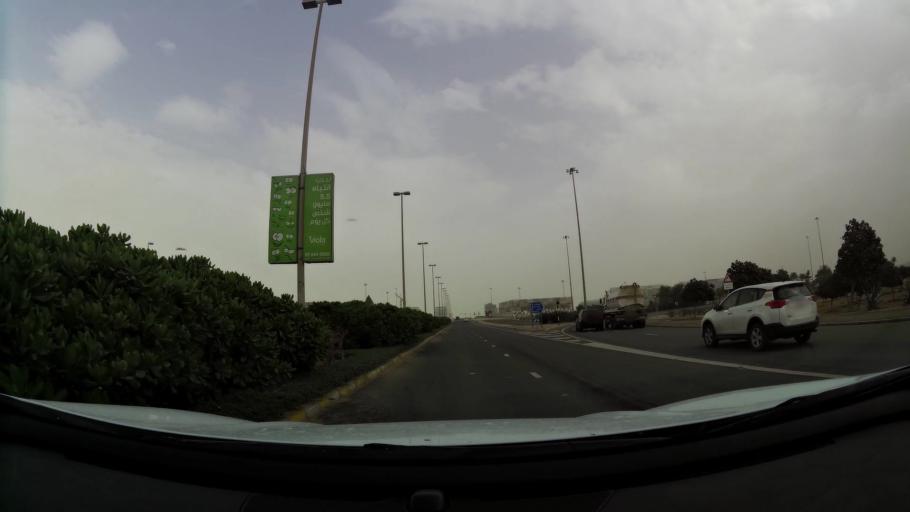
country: AE
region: Abu Dhabi
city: Abu Dhabi
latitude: 24.4426
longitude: 54.6013
